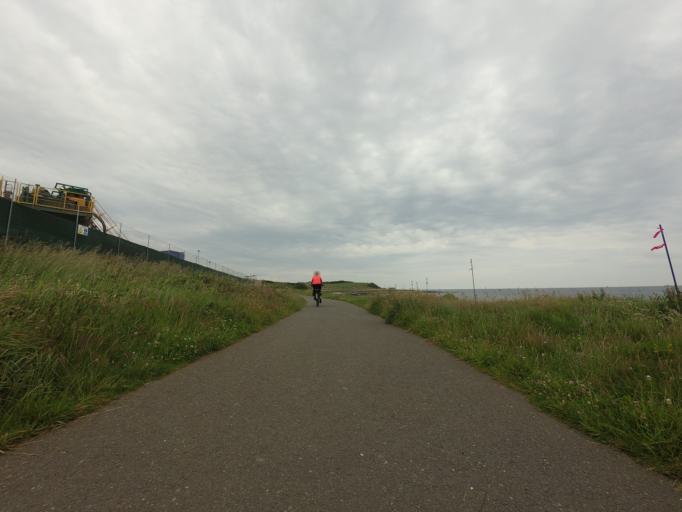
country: GB
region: Scotland
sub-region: Aberdeenshire
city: Whitehills
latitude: 57.6737
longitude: -2.5646
